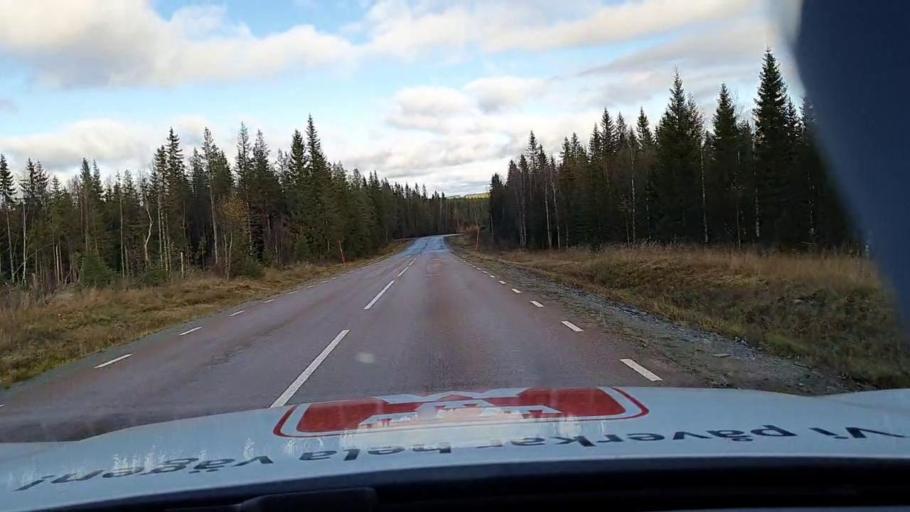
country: SE
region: Jaemtland
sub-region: Krokoms Kommun
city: Valla
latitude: 63.1511
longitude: 13.9574
